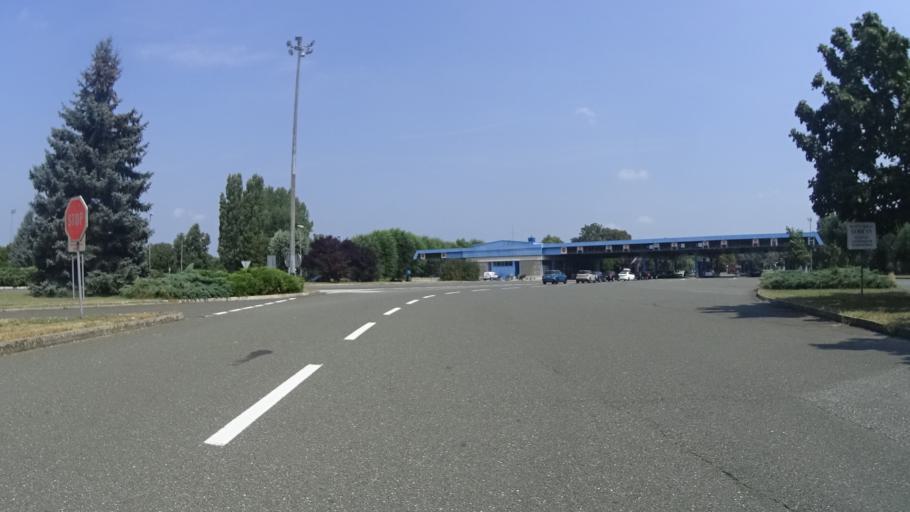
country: HR
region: Medimurska
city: Gorican
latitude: 46.4172
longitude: 16.6892
